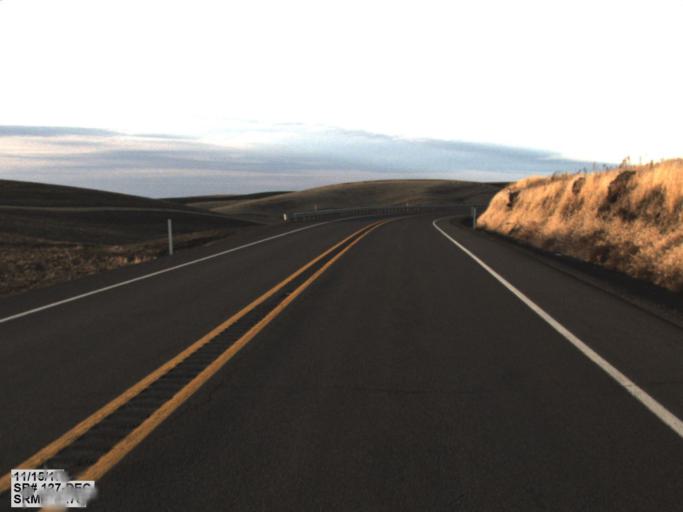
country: US
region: Washington
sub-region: Garfield County
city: Pomeroy
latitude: 46.7159
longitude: -117.7733
